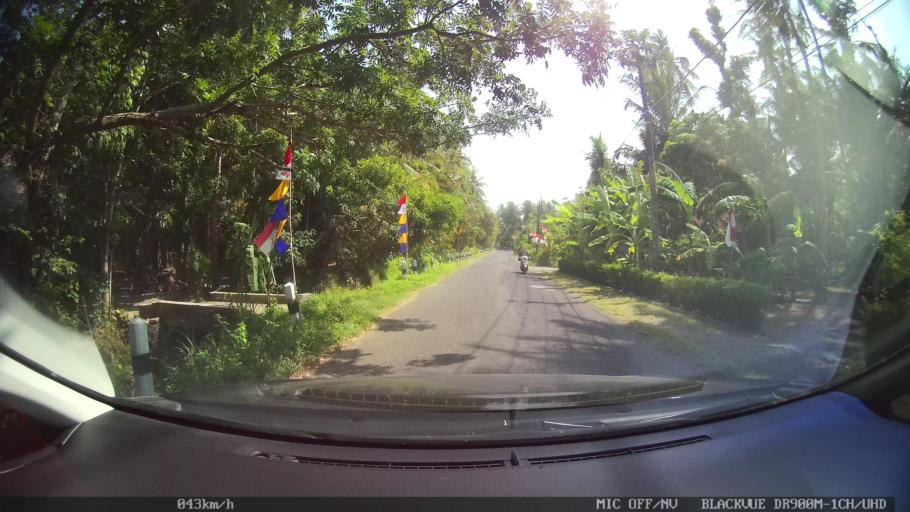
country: ID
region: Daerah Istimewa Yogyakarta
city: Srandakan
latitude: -7.9137
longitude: 110.1539
